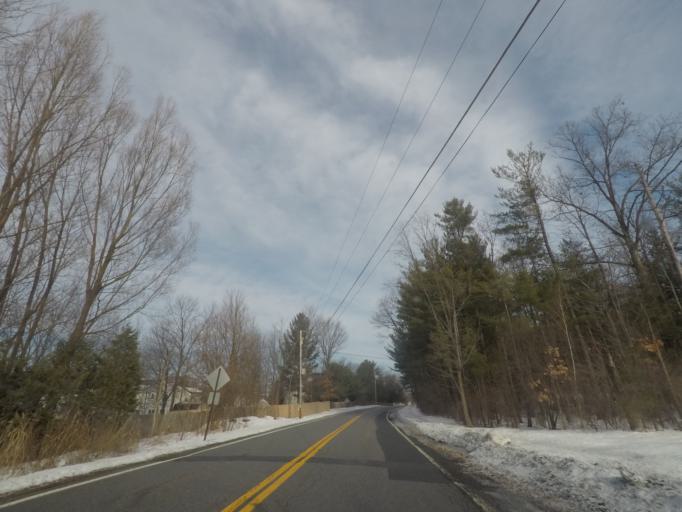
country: US
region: New York
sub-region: Saratoga County
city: Country Knolls
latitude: 42.8765
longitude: -73.7514
